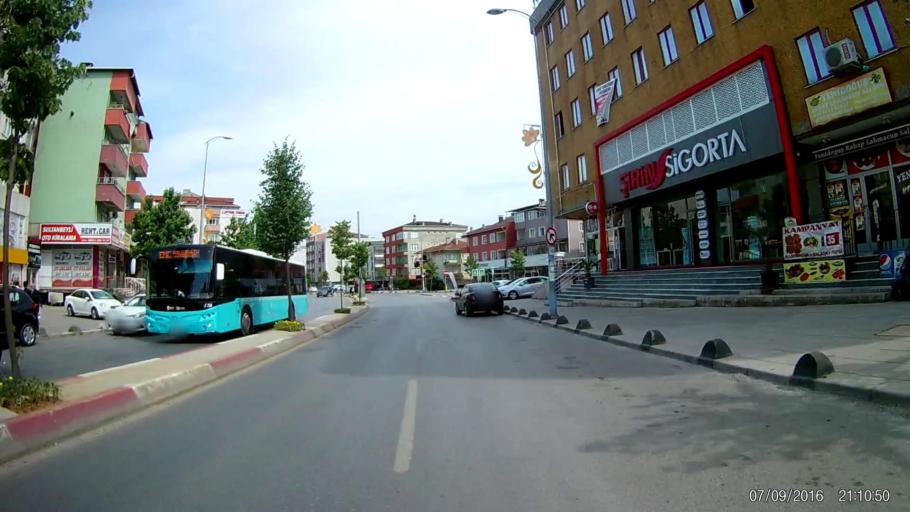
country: TR
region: Istanbul
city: Sultanbeyli
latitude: 40.9654
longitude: 29.2761
